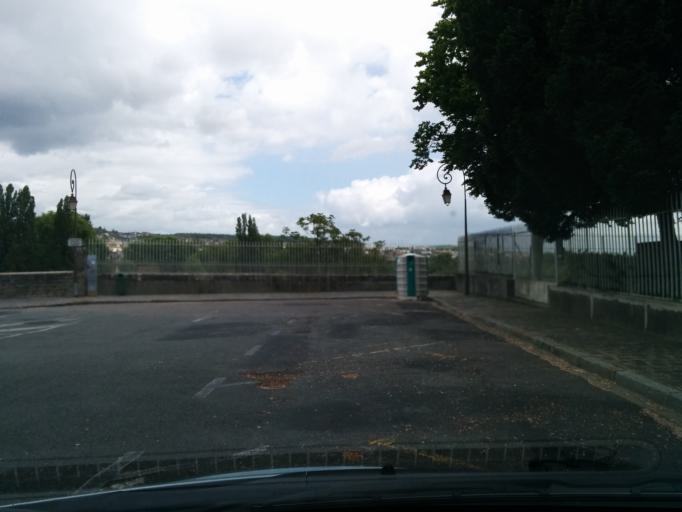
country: FR
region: Ile-de-France
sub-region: Departement des Yvelines
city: Mantes-la-Jolie
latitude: 48.9898
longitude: 1.7210
